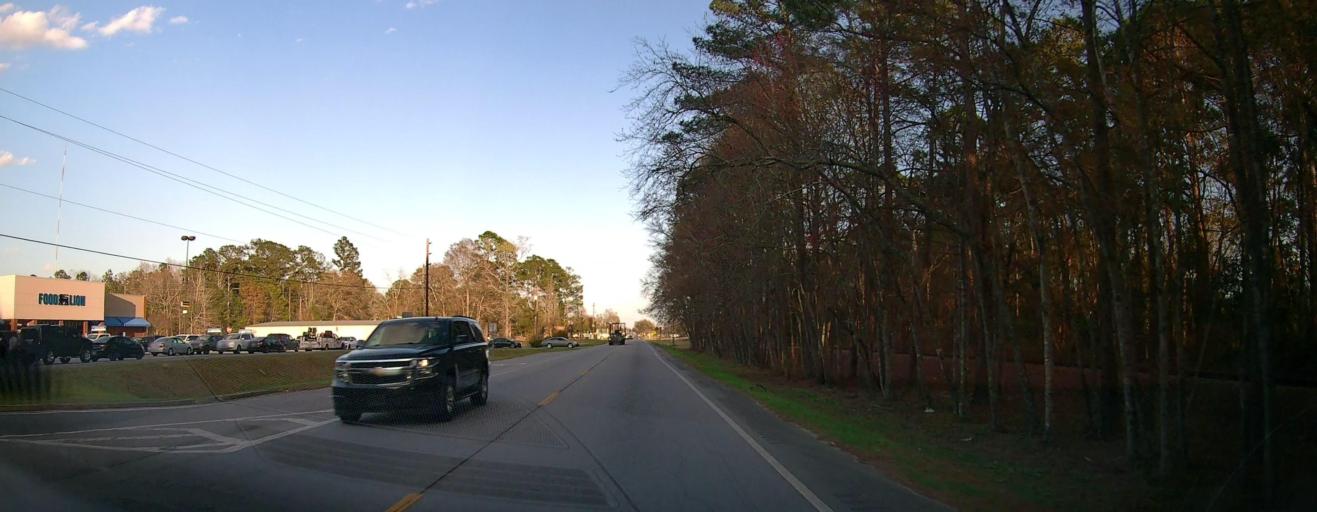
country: US
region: Georgia
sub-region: Bryan County
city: Pembroke
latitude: 32.1364
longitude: -81.6327
